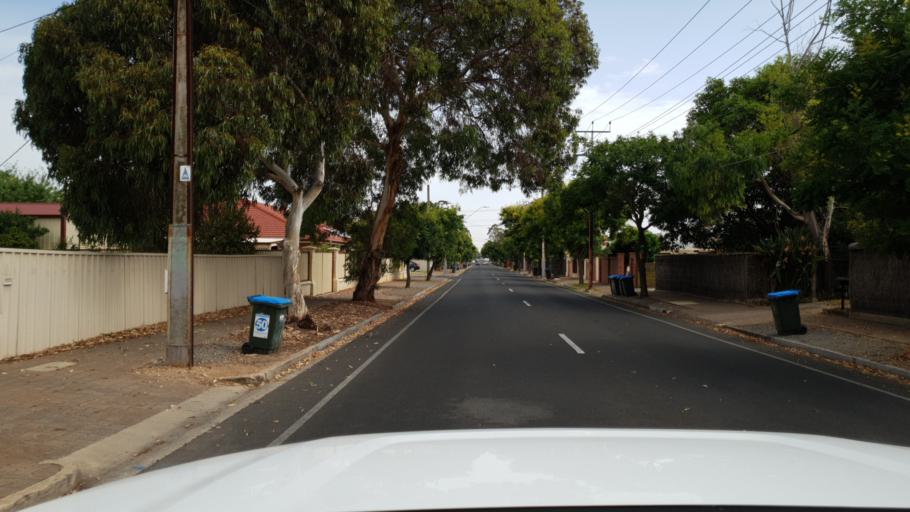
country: AU
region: South Australia
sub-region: Mitcham
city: Clarence Gardens
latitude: -34.9711
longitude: 138.5822
